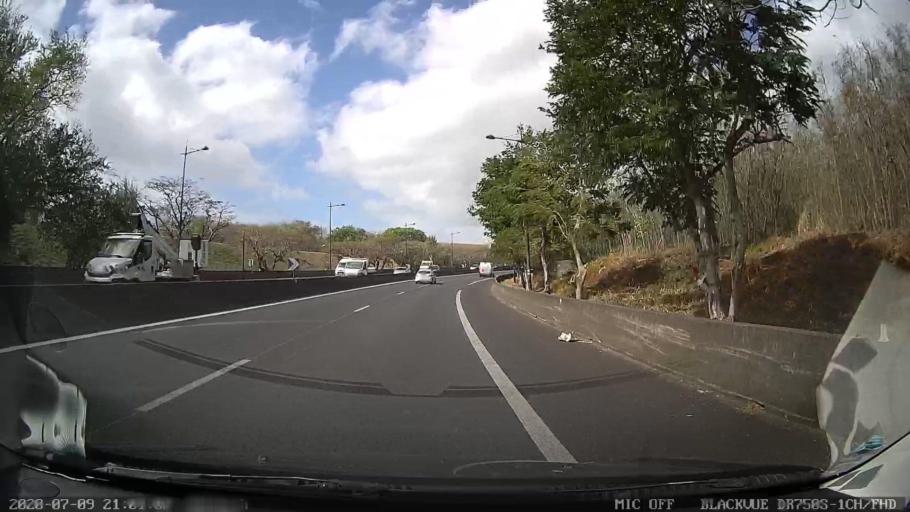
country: RE
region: Reunion
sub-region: Reunion
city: Saint-Denis
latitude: -20.8854
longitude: 55.4983
